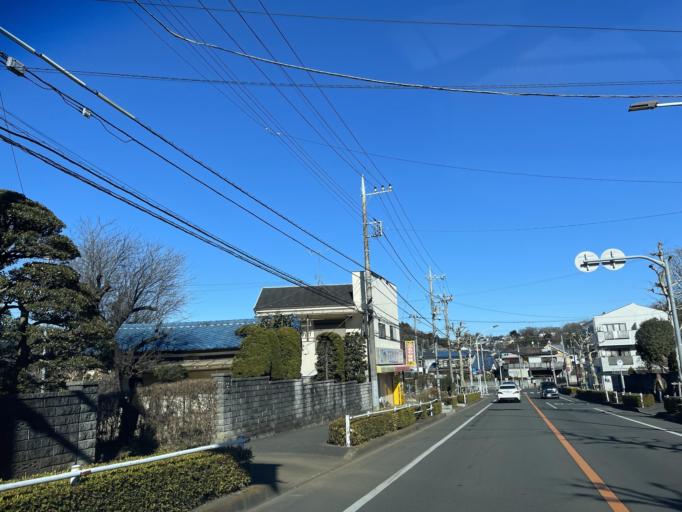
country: JP
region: Tokyo
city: Higashimurayama-shi
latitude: 35.7524
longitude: 139.4229
